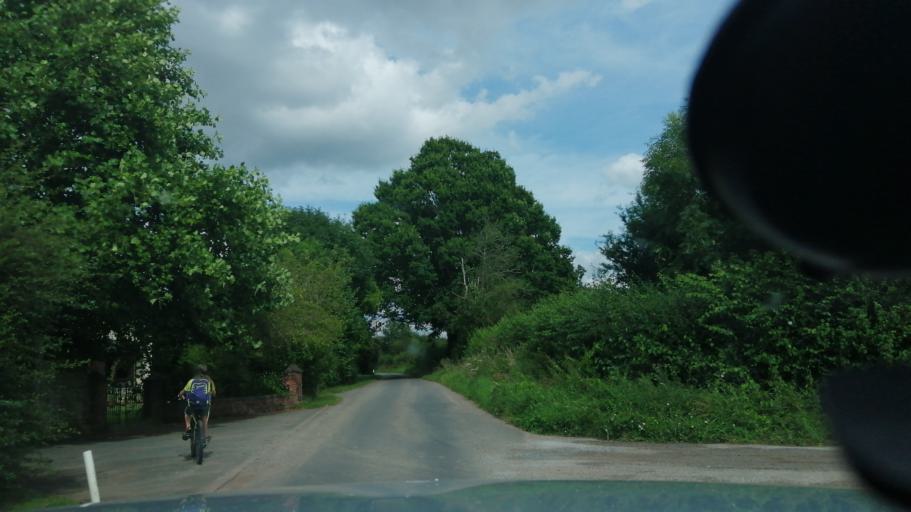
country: GB
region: England
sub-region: Herefordshire
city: Thruxton
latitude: 52.0187
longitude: -2.7935
